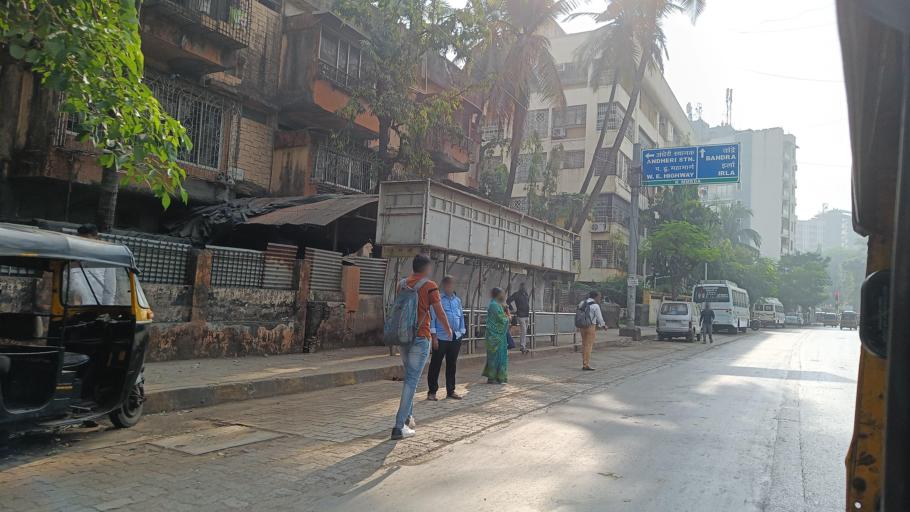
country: IN
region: Maharashtra
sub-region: Mumbai Suburban
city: Mumbai
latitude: 19.1138
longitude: 72.8368
